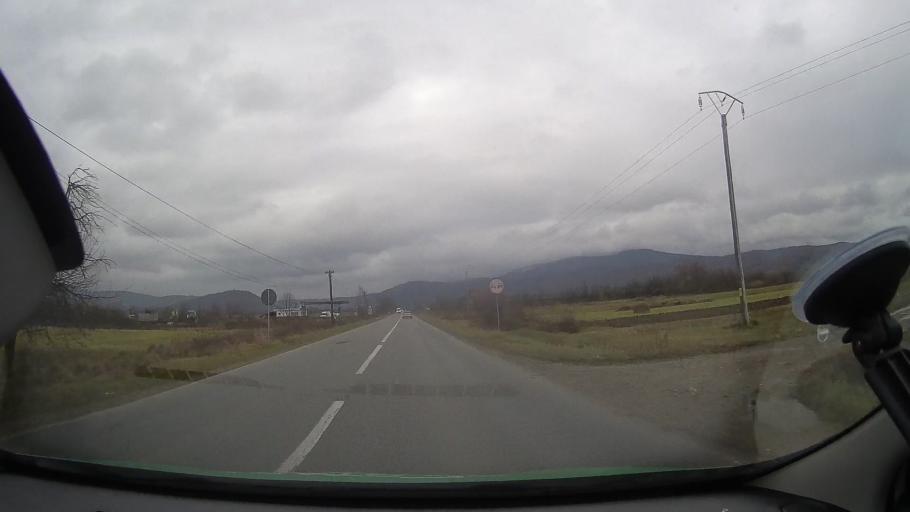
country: RO
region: Arad
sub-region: Comuna Buteni
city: Buteni
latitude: 46.3221
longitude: 22.1285
